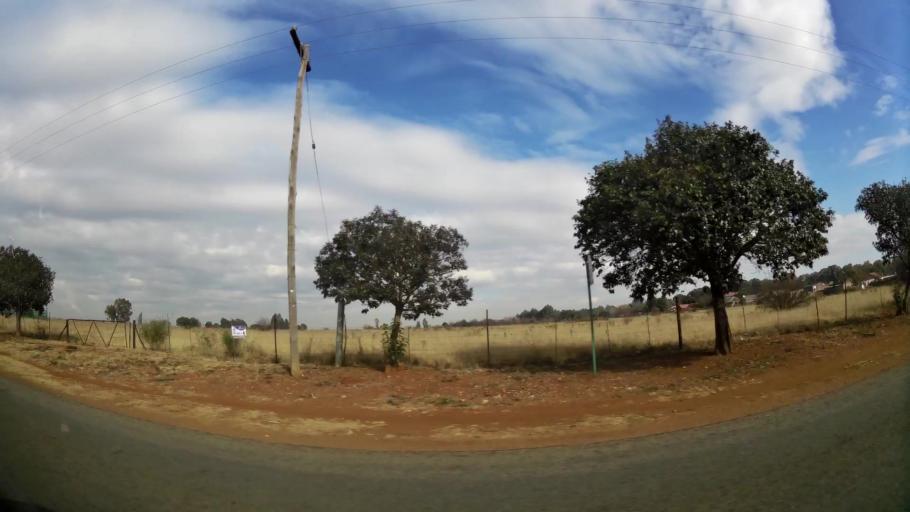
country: ZA
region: Gauteng
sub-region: Sedibeng District Municipality
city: Meyerton
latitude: -26.5523
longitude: 28.0608
